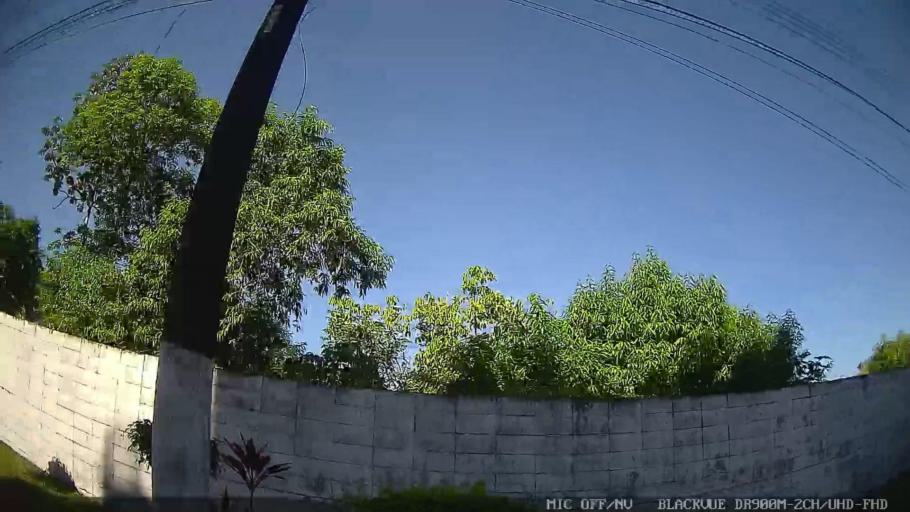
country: BR
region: Sao Paulo
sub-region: Guaruja
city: Guaruja
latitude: -23.9877
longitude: -46.2016
